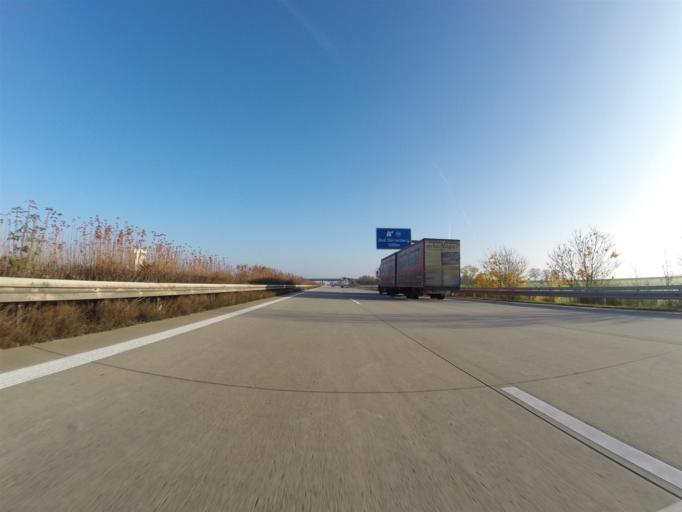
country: DE
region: Saxony-Anhalt
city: Tollwitz
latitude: 51.2805
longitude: 12.1219
